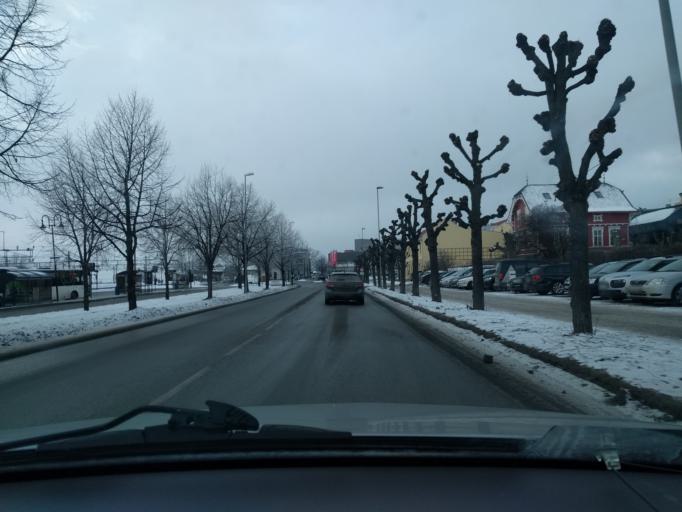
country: NO
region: Hedmark
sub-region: Hamar
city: Hamar
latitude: 60.7915
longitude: 11.0812
